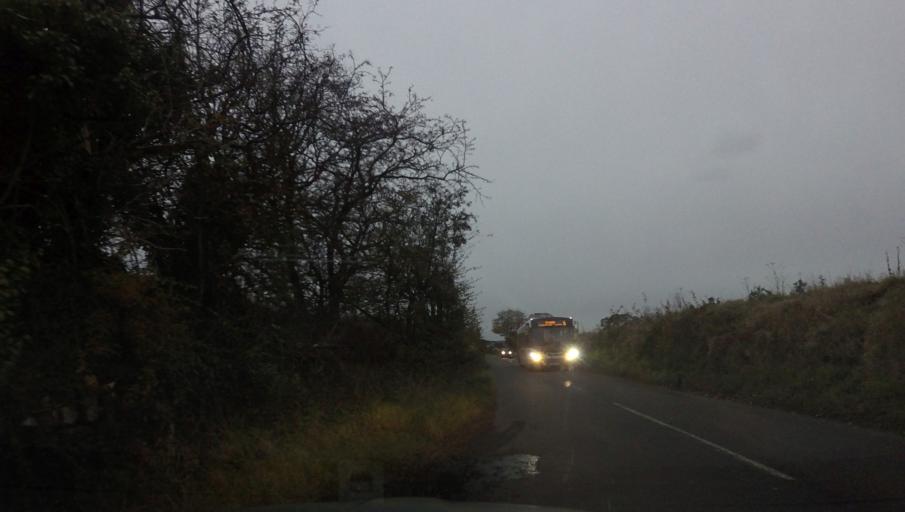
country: GB
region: Scotland
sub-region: Fife
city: Crossford
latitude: 56.0422
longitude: -3.5059
